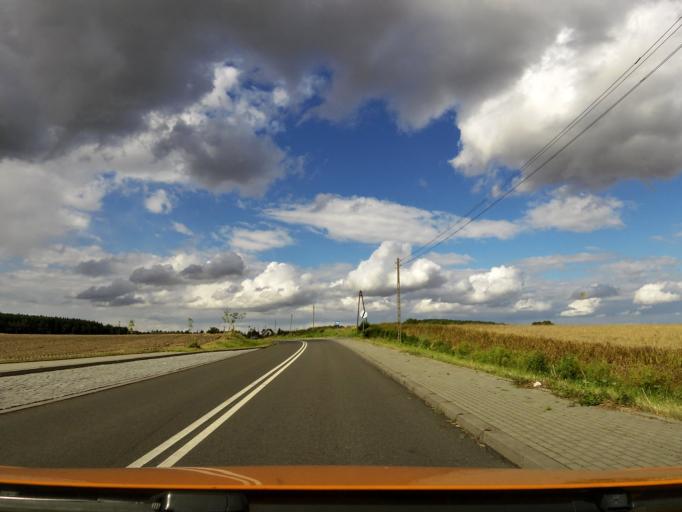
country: PL
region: West Pomeranian Voivodeship
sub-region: Powiat kolobrzeski
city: Ryman
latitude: 53.9723
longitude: 15.4903
